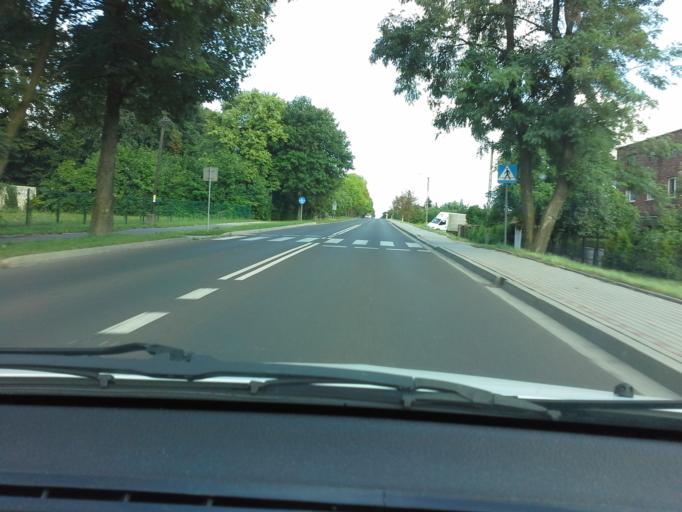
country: PL
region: Lesser Poland Voivodeship
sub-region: Powiat chrzanowski
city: Trzebinia
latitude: 50.1492
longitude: 19.4935
